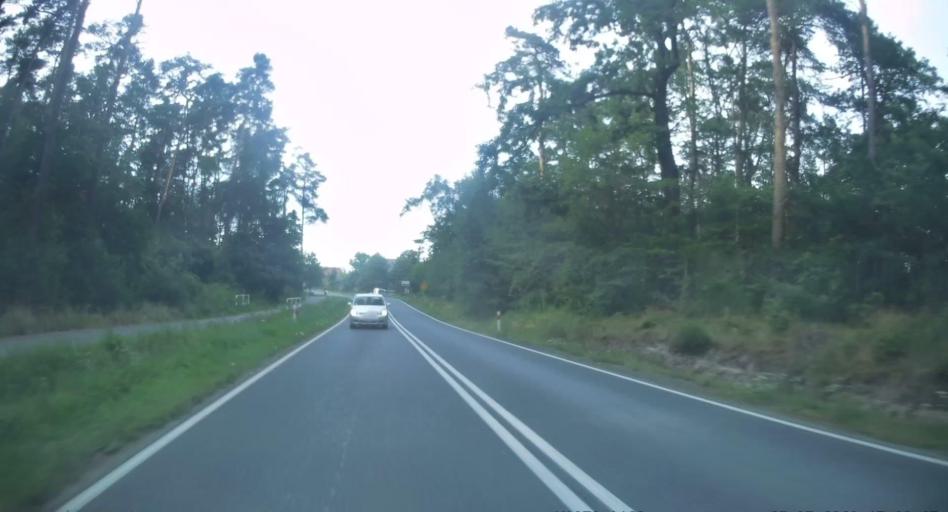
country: PL
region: Lesser Poland Voivodeship
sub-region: Powiat brzeski
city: Przyborow
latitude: 50.0568
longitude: 20.6395
